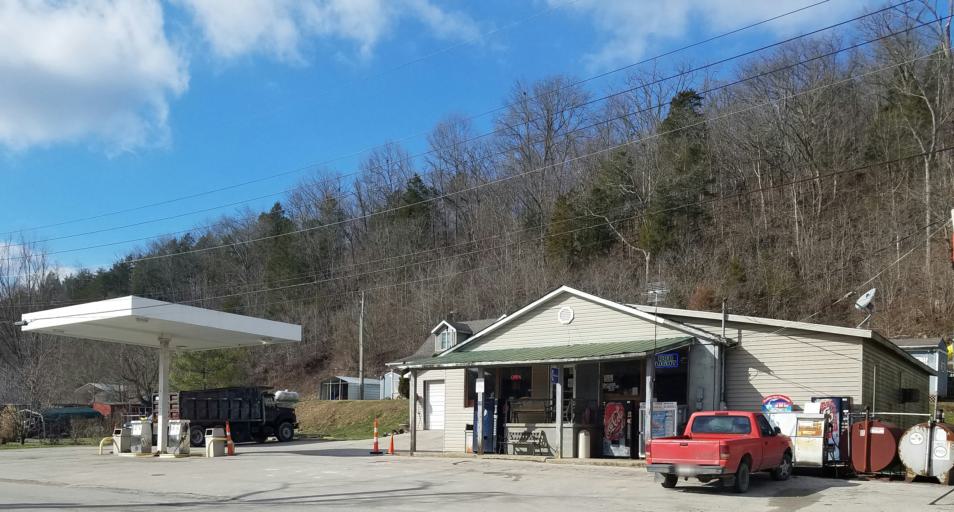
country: US
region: Kentucky
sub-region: Owen County
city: Owenton
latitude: 38.4240
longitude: -84.8819
